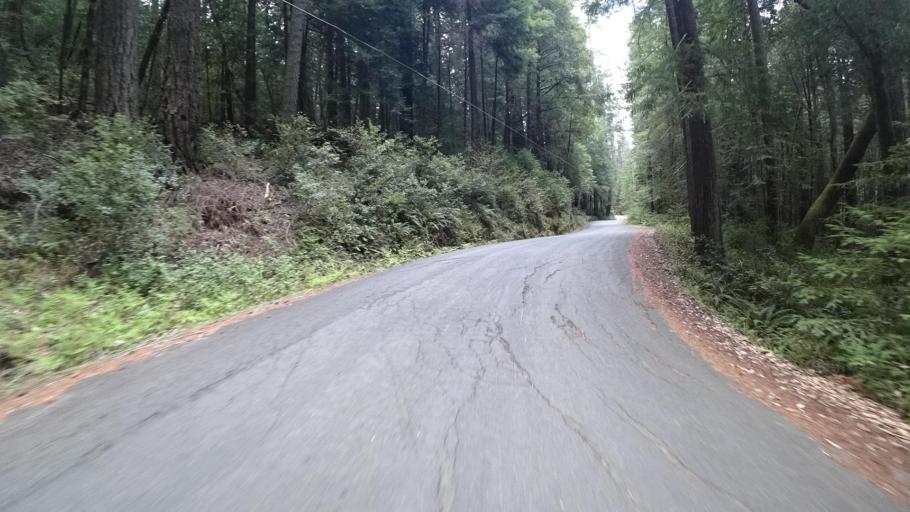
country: US
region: California
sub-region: Humboldt County
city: Redway
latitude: 39.9996
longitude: -123.9278
